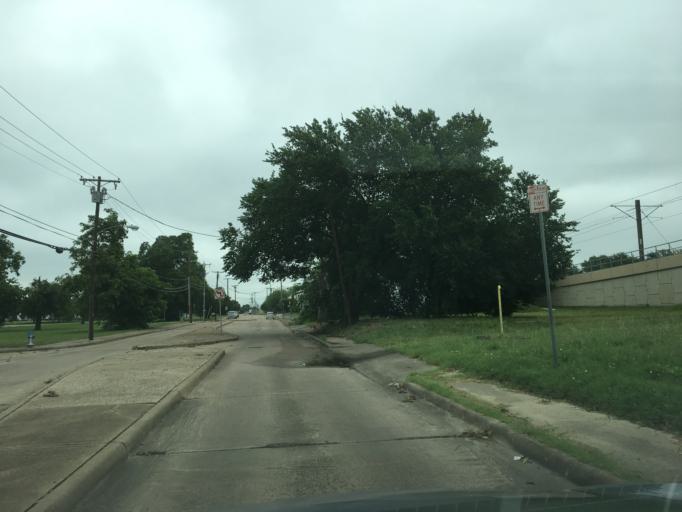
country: US
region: Texas
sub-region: Dallas County
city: Richardson
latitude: 32.9501
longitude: -96.7319
